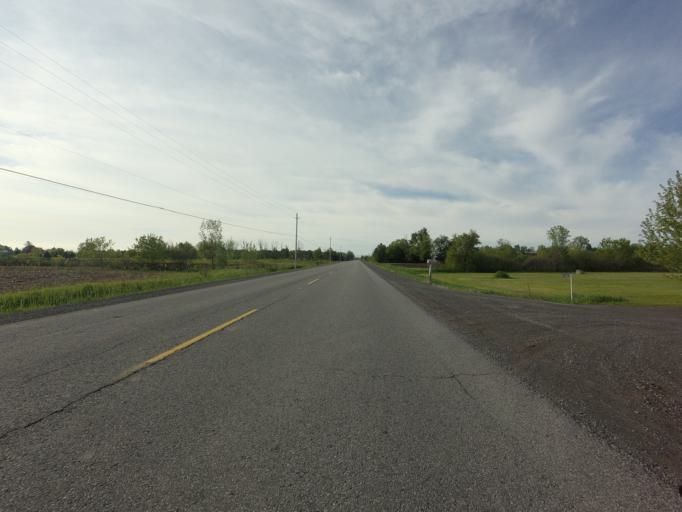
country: CA
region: Ontario
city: Ottawa
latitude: 45.2960
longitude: -75.4514
